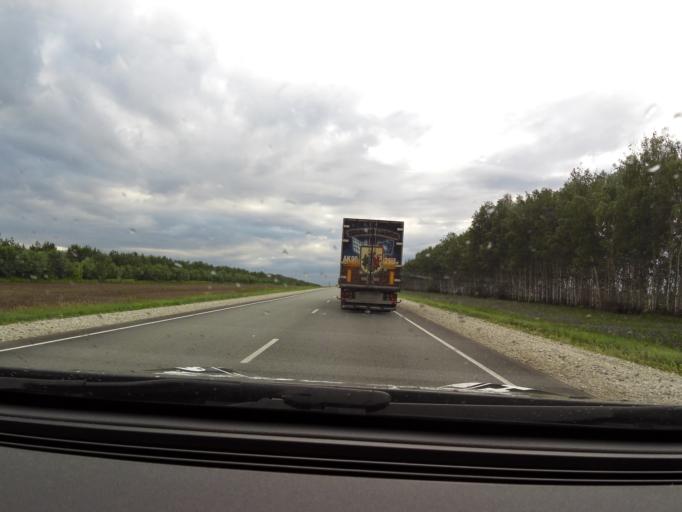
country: RU
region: Tatarstan
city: Nizhniye Vyazovyye
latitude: 55.7249
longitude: 48.4321
